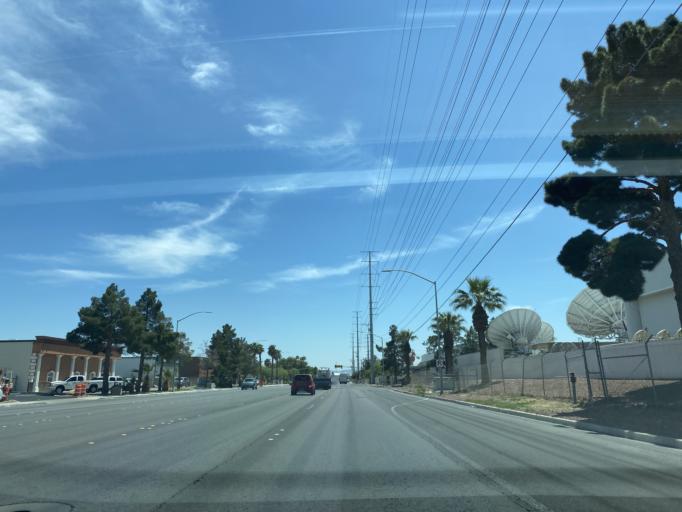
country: US
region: Nevada
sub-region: Clark County
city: North Las Vegas
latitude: 36.2368
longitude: -115.1168
